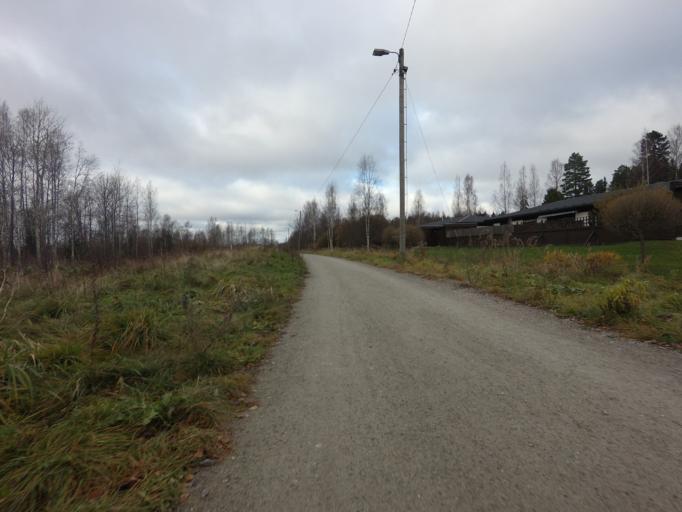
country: FI
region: Uusimaa
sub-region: Helsinki
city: Kauniainen
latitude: 60.1720
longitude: 24.7032
